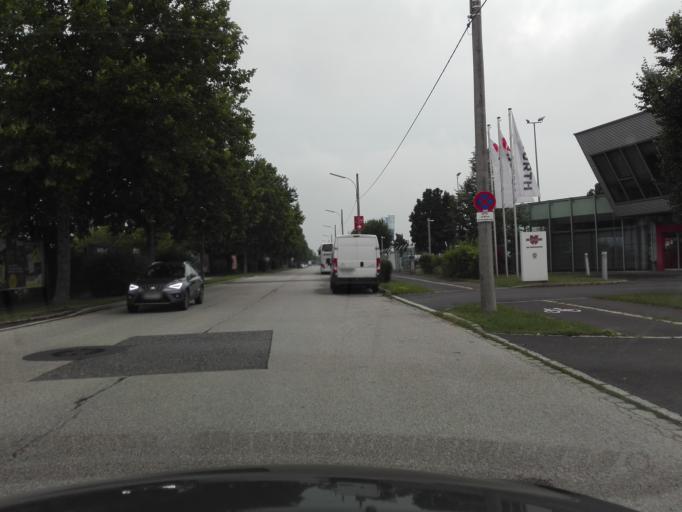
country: AT
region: Upper Austria
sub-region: Politischer Bezirk Linz-Land
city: Ansfelden
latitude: 48.2443
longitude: 14.2939
